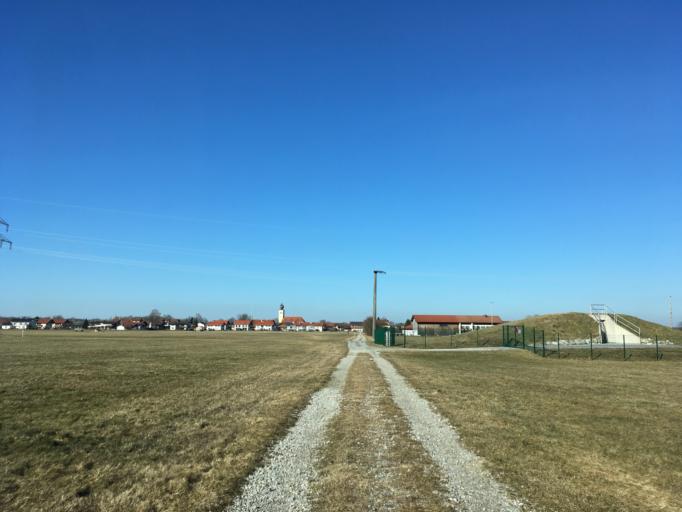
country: DE
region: Bavaria
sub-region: Upper Bavaria
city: Irschenberg
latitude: 47.8567
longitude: 11.9455
